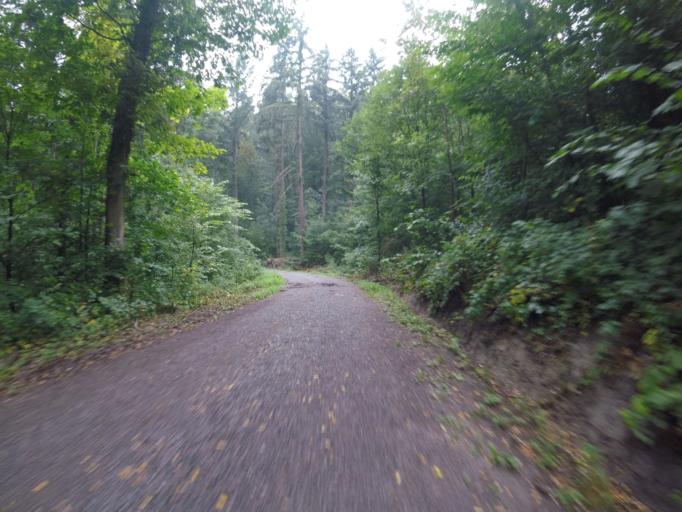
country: DE
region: Baden-Wuerttemberg
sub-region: Regierungsbezirk Stuttgart
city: Oppenweiler
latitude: 48.9836
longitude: 9.4388
